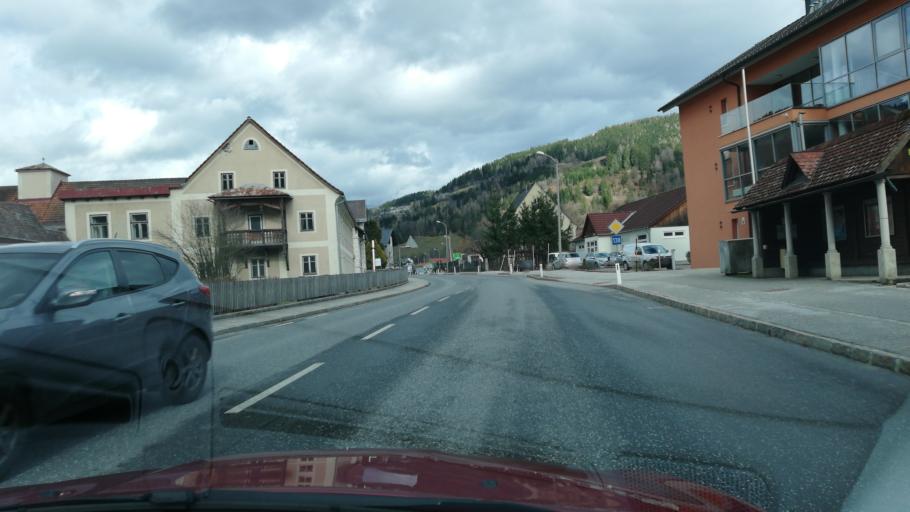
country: AT
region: Upper Austria
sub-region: Politischer Bezirk Kirchdorf an der Krems
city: Rossleithen
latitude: 47.6648
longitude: 14.3408
